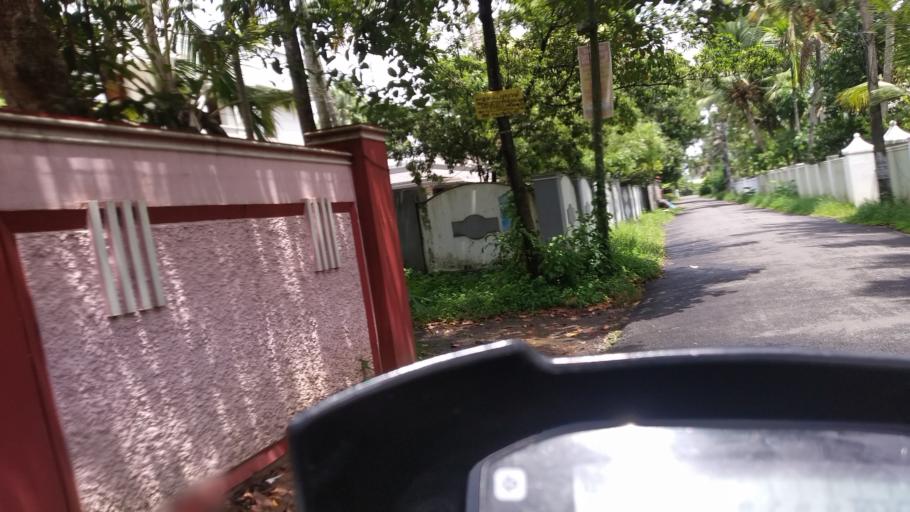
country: IN
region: Kerala
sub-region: Ernakulam
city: Elur
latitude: 10.0653
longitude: 76.2100
